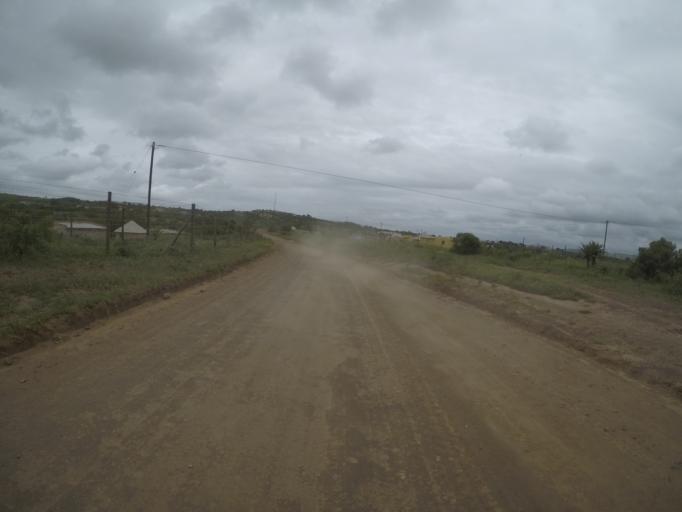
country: ZA
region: KwaZulu-Natal
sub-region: uThungulu District Municipality
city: Empangeni
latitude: -28.5965
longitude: 31.8385
